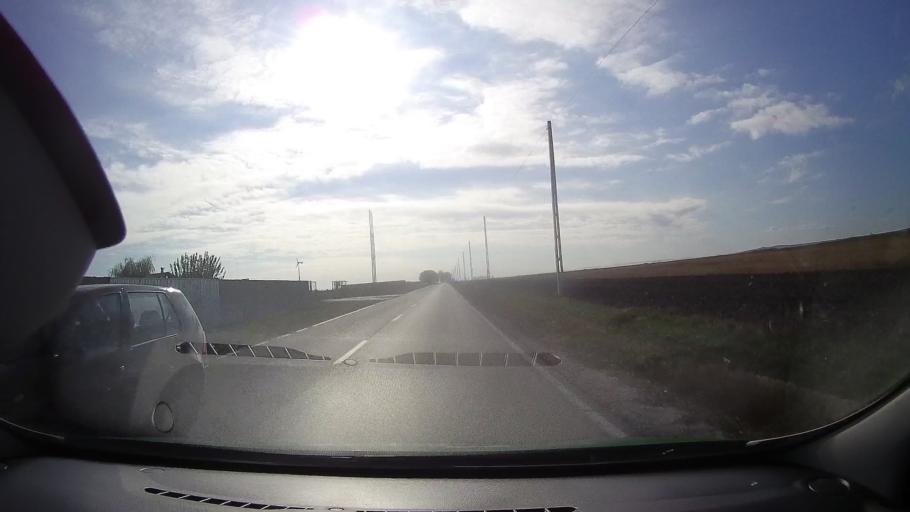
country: RO
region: Tulcea
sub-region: Comuna Valea Nucarilor
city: Agighiol
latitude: 45.0208
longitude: 28.8826
